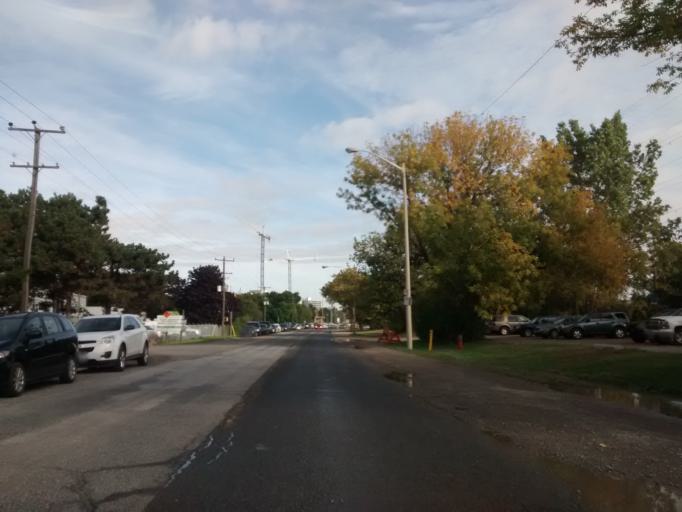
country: CA
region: Ontario
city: Hamilton
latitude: 43.3115
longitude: -79.8011
